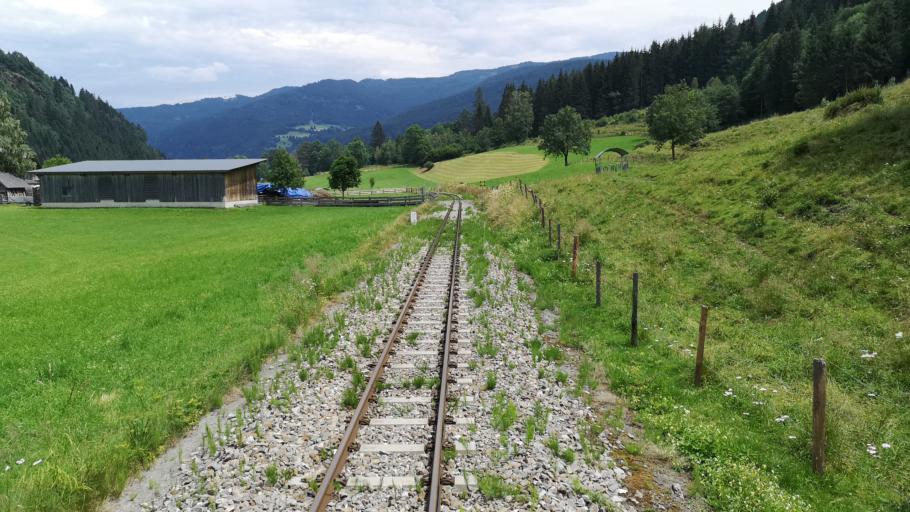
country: AT
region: Styria
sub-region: Politischer Bezirk Murau
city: Stadl an der Mur
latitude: 47.0828
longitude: 13.9568
